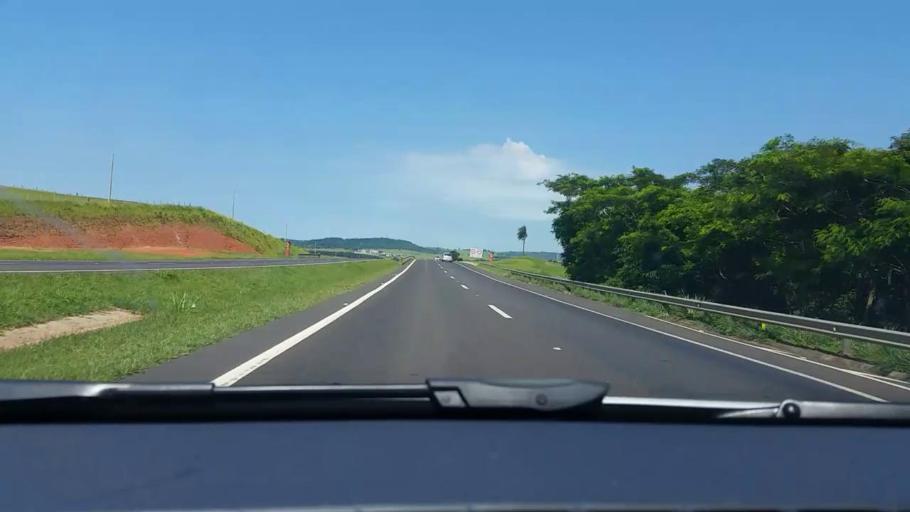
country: BR
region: Sao Paulo
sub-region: Bauru
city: Bauru
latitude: -22.3937
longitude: -49.0820
